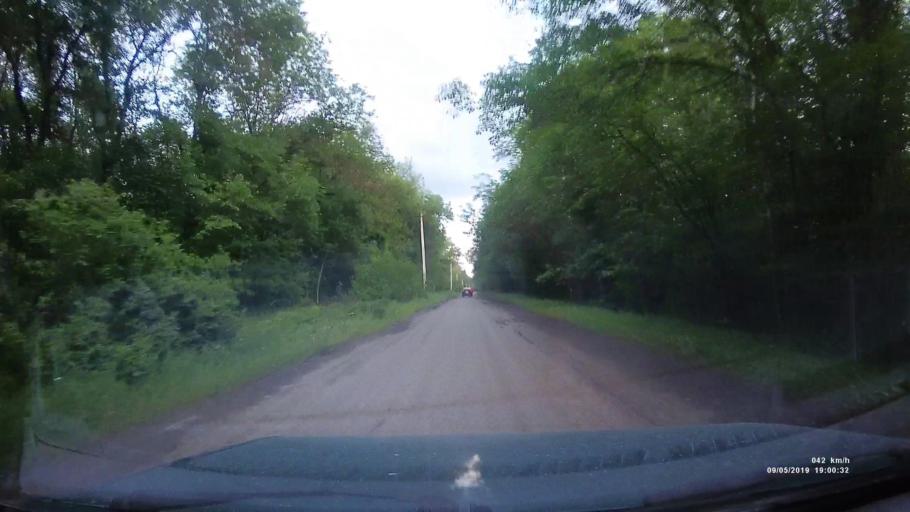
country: RU
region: Krasnodarskiy
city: Kanelovskaya
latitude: 46.7516
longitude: 39.1367
